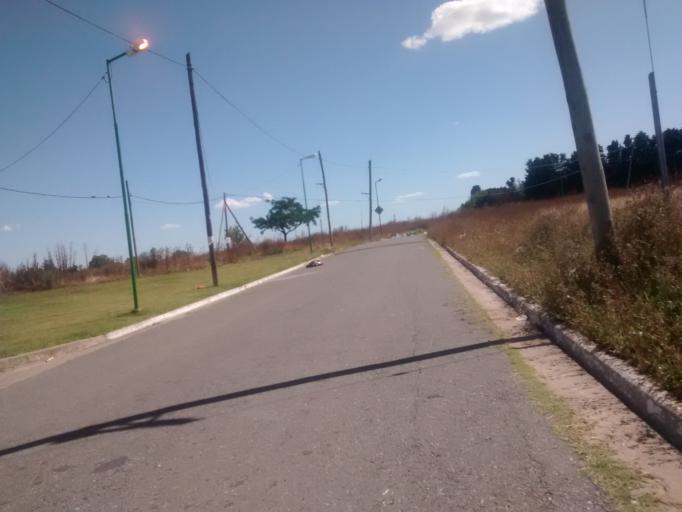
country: AR
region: Buenos Aires
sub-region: Partido de La Plata
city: La Plata
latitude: -34.9356
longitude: -57.9049
